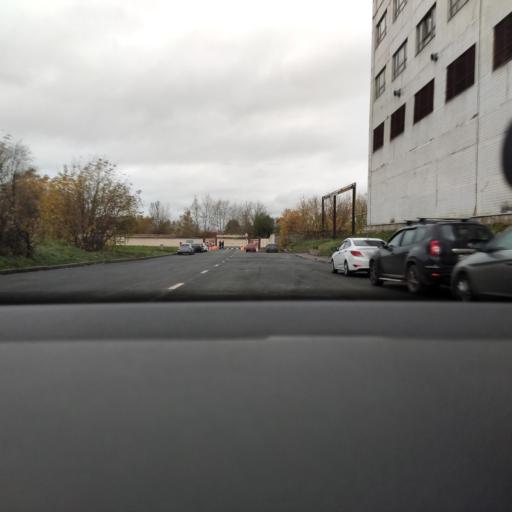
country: RU
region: Moscow
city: Mikhalkovo
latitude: 55.6770
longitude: 37.4281
